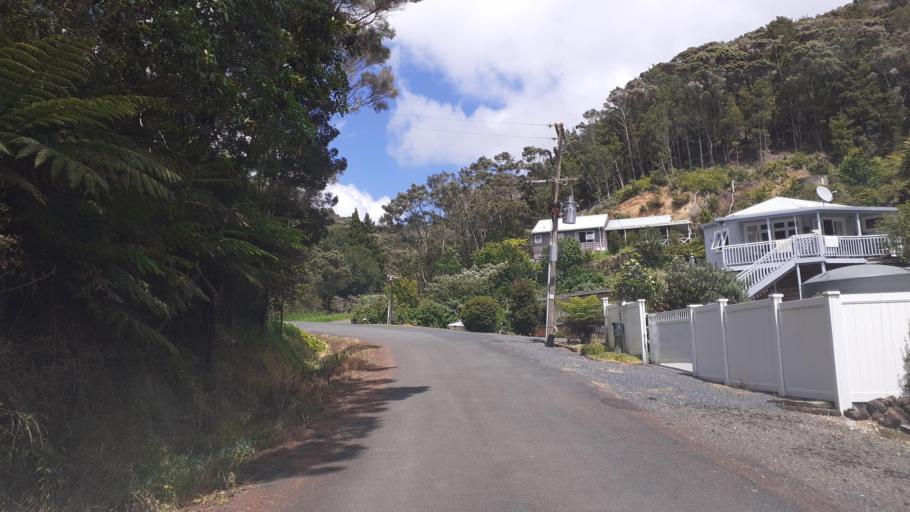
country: NZ
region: Northland
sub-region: Far North District
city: Paihia
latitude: -35.3088
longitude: 174.1116
